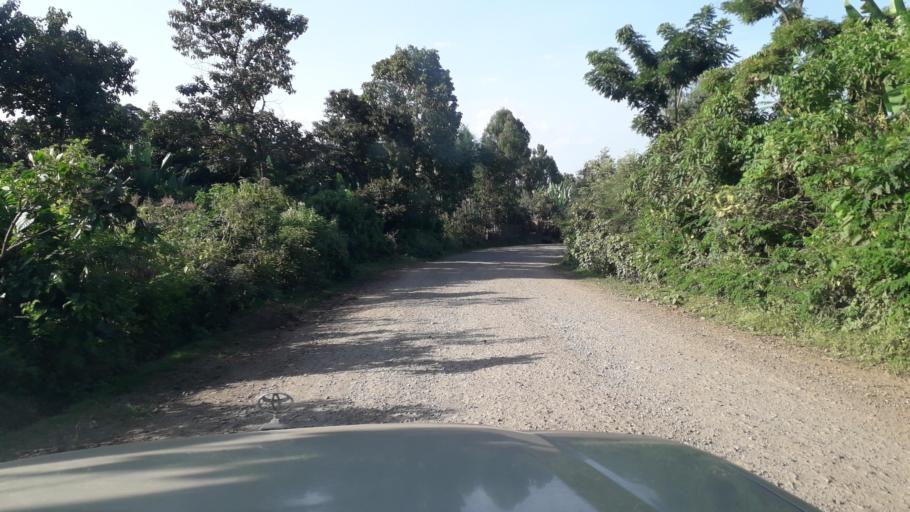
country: ET
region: Oromiya
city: Jima
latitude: 7.4645
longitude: 36.8745
